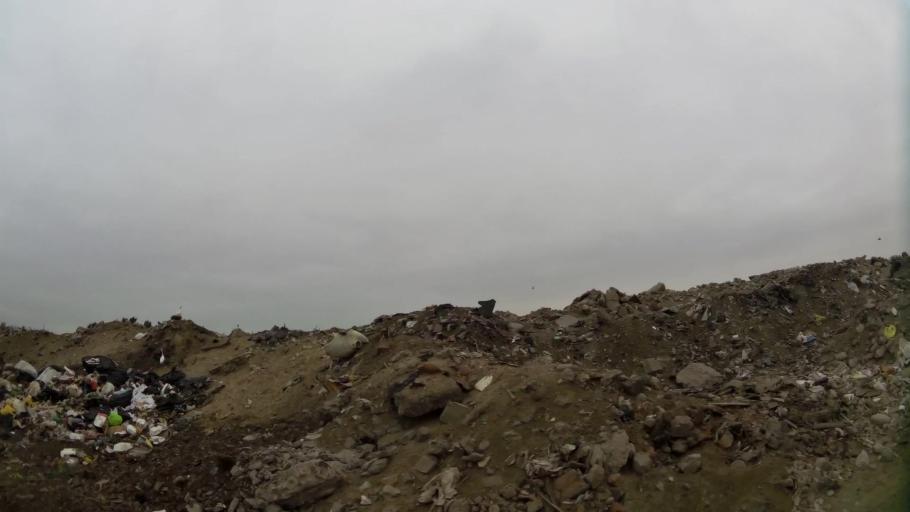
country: PE
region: Ica
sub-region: Provincia de Pisco
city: Pisco
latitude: -13.7501
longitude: -76.1906
